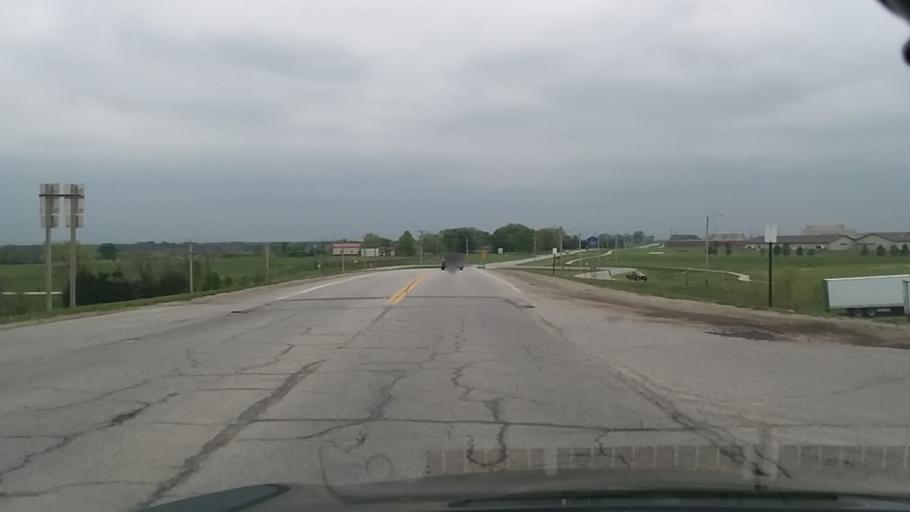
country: US
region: Kansas
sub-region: Douglas County
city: Eudora
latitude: 38.9289
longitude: -95.0944
